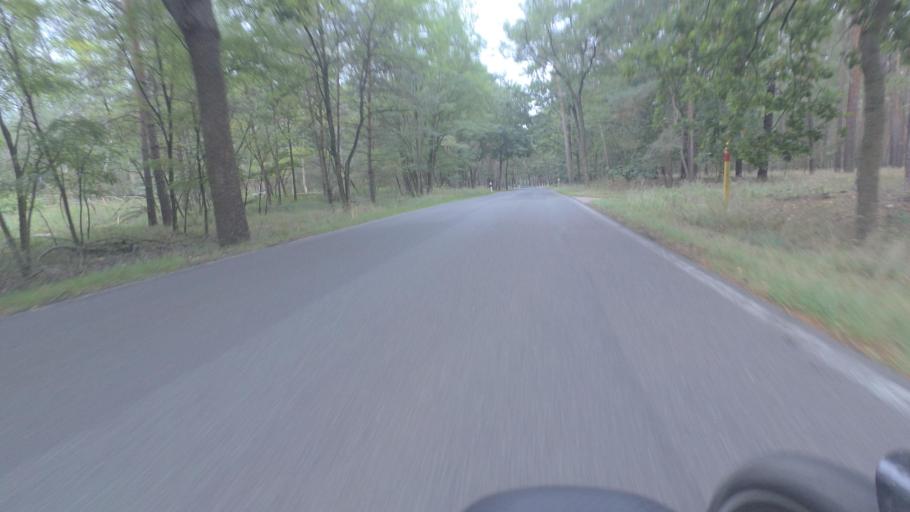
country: DE
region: Brandenburg
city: Luckenwalde
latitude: 52.1315
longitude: 13.1905
